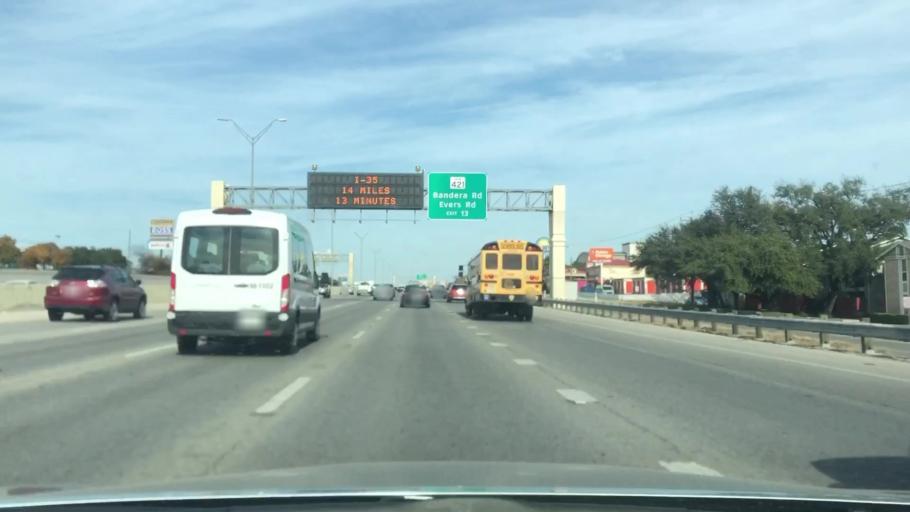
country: US
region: Texas
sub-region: Bexar County
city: Leon Valley
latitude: 29.4732
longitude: -98.6120
